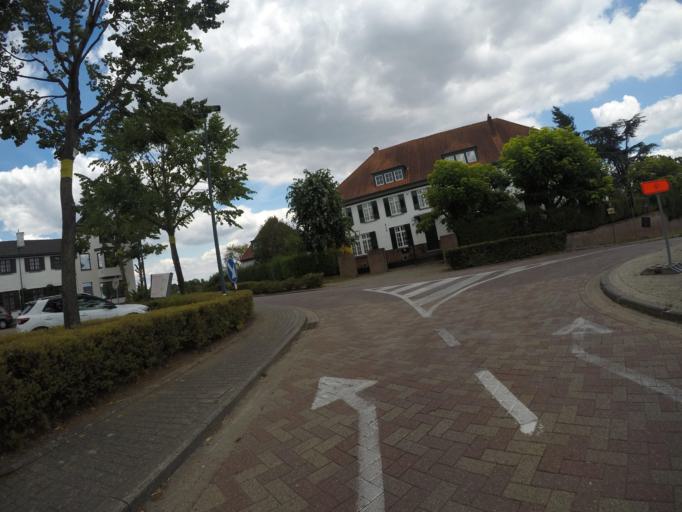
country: BE
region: Flanders
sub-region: Provincie Vlaams-Brabant
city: Ledeberg
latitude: 50.8428
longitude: 4.0866
